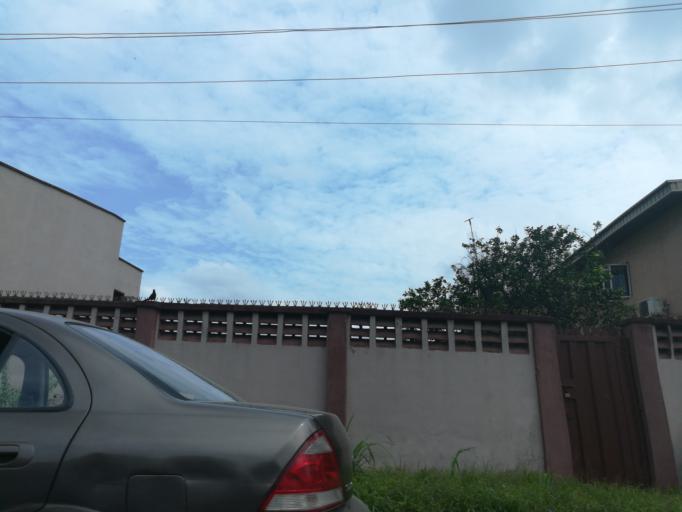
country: NG
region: Lagos
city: Somolu
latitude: 6.5479
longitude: 3.3885
